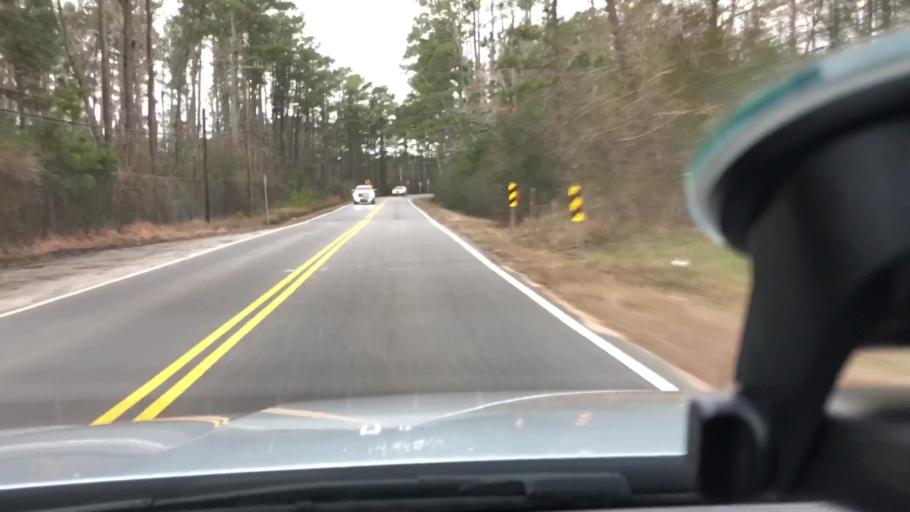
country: US
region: Virginia
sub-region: City of Virginia Beach
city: Virginia Beach
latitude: 36.7324
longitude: -75.9715
